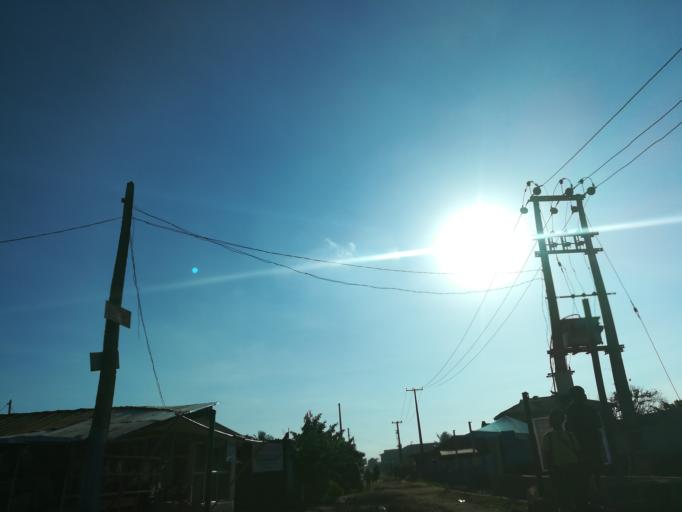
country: NG
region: Lagos
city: Ikorodu
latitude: 6.5801
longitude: 3.5257
